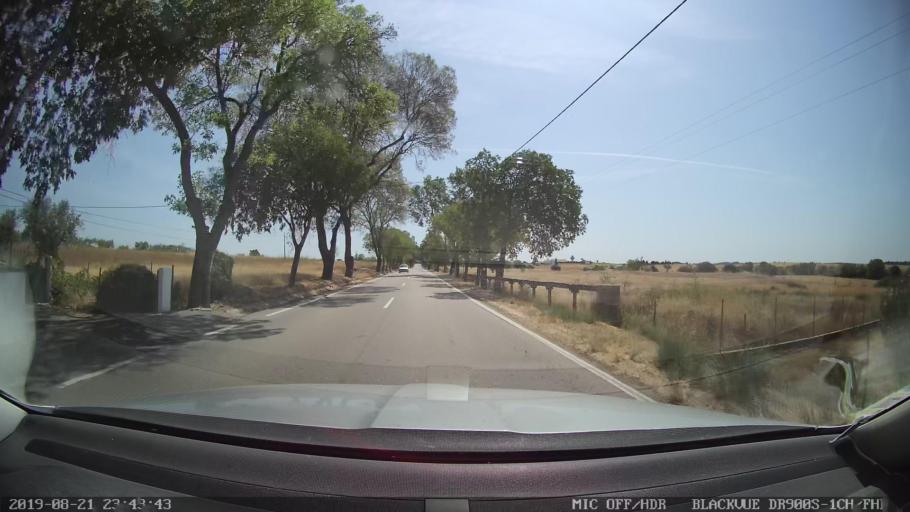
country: PT
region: Castelo Branco
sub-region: Idanha-A-Nova
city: Idanha-a-Nova
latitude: 39.8489
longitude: -7.2904
